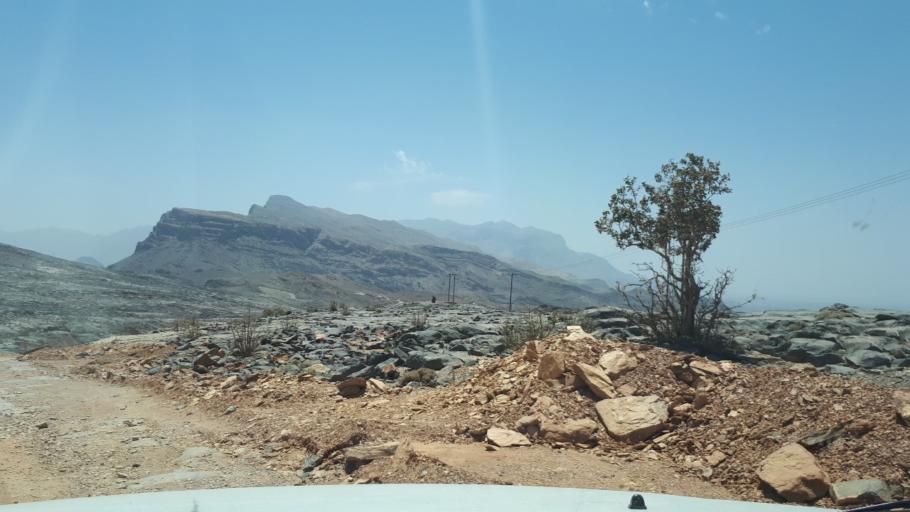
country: OM
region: Al Batinah
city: Rustaq
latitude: 23.2491
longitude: 57.1615
